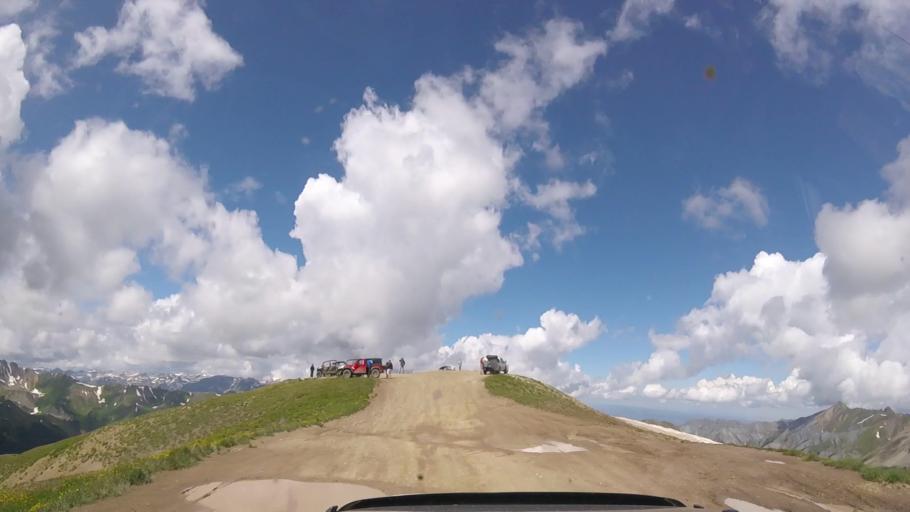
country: US
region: Colorado
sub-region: Ouray County
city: Ouray
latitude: 37.9698
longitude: -107.5928
